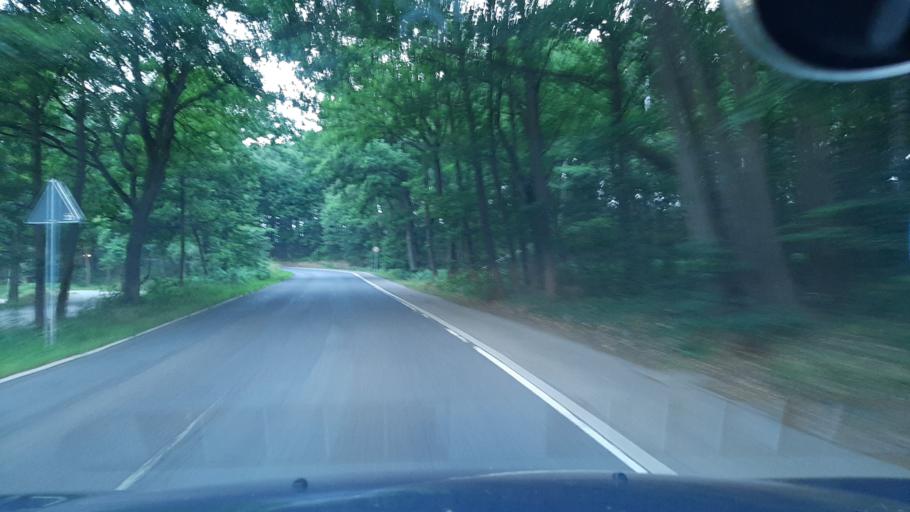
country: DE
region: North Rhine-Westphalia
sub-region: Regierungsbezirk Koln
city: Mechernich
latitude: 50.6055
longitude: 6.6783
